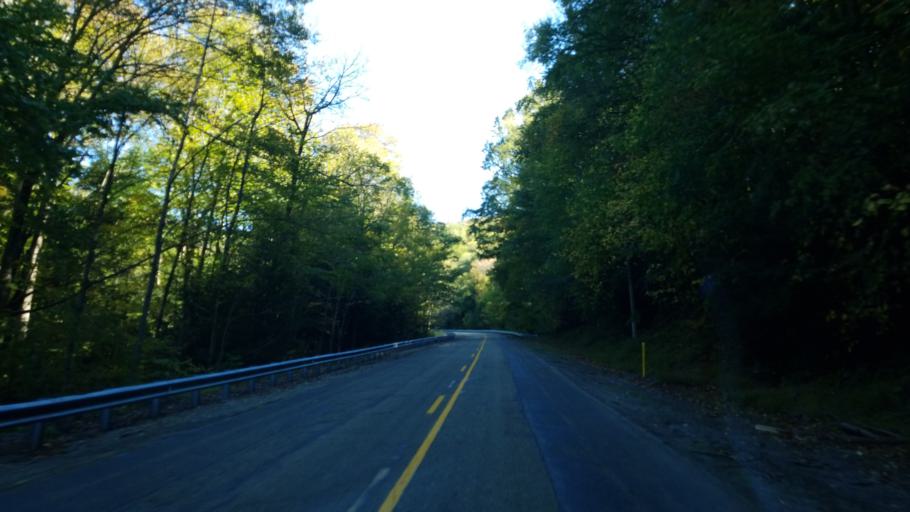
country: US
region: Pennsylvania
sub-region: Clearfield County
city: Shiloh
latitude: 41.2519
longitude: -78.3805
